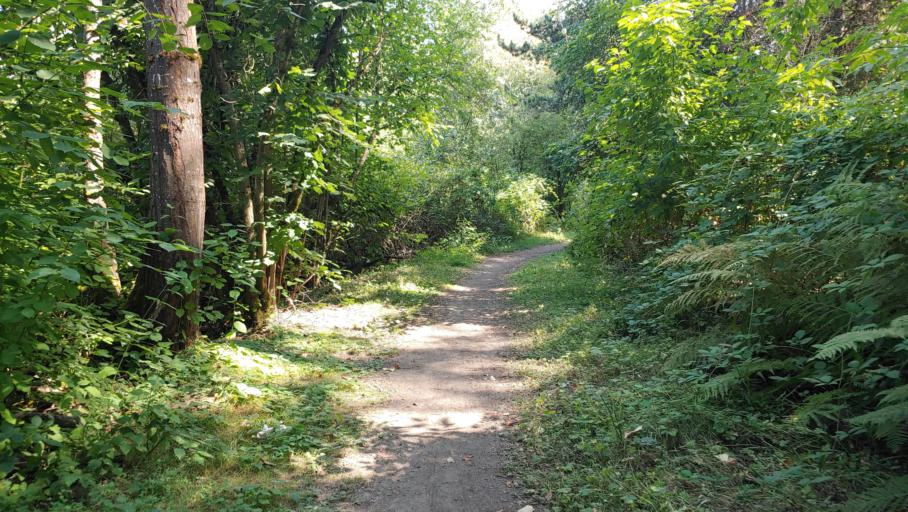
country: US
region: Washington
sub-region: King County
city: Bryn Mawr-Skyway
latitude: 47.4752
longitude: -122.2390
